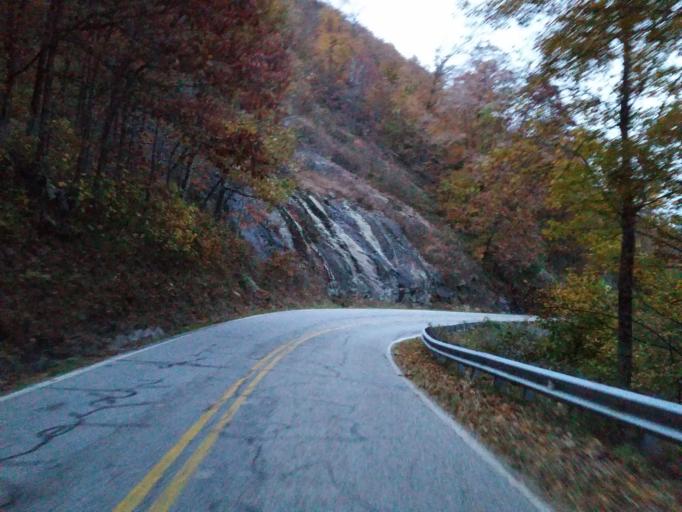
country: US
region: Georgia
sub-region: Lumpkin County
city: Dahlonega
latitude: 34.6769
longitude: -83.9984
